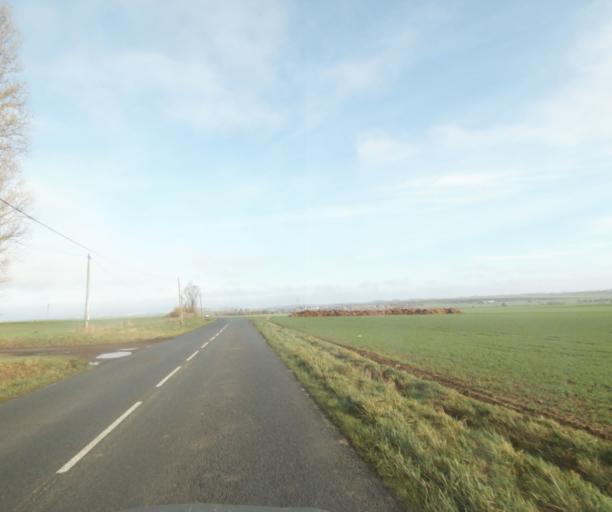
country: FR
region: Nord-Pas-de-Calais
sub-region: Departement du Nord
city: Thiant
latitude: 50.2779
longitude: 3.4383
